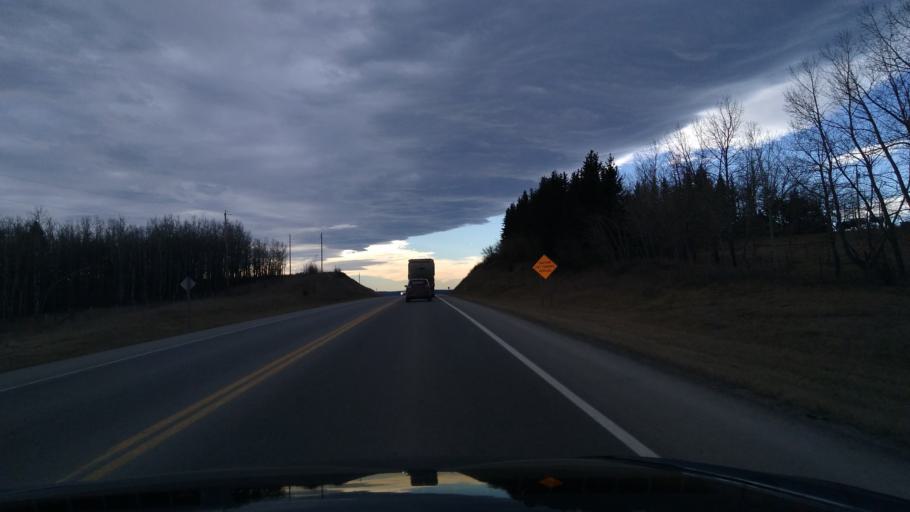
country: CA
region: Alberta
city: Cochrane
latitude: 51.1038
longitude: -114.4668
